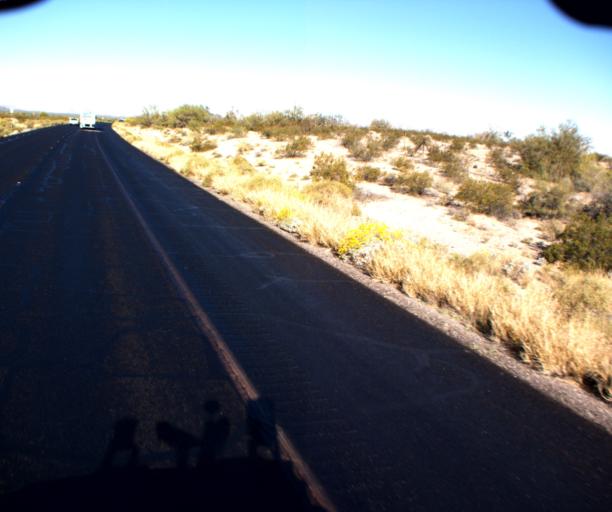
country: US
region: Arizona
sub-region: Pinal County
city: Maricopa
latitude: 32.8368
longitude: -112.2083
